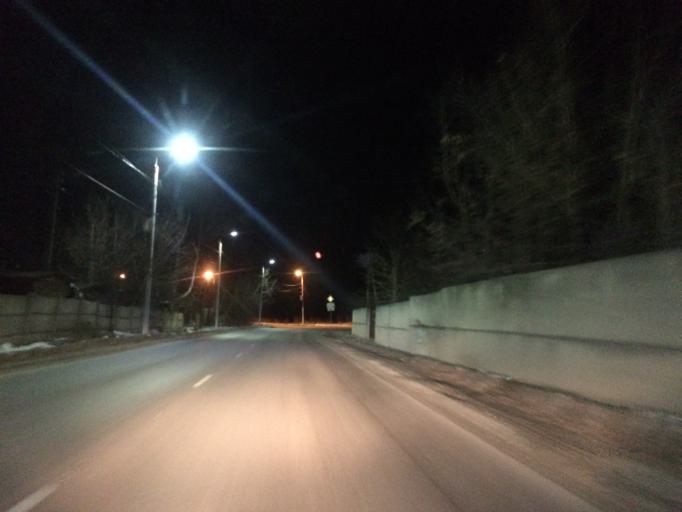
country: RU
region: Tula
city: Mendeleyevskiy
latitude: 54.1458
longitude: 37.5992
